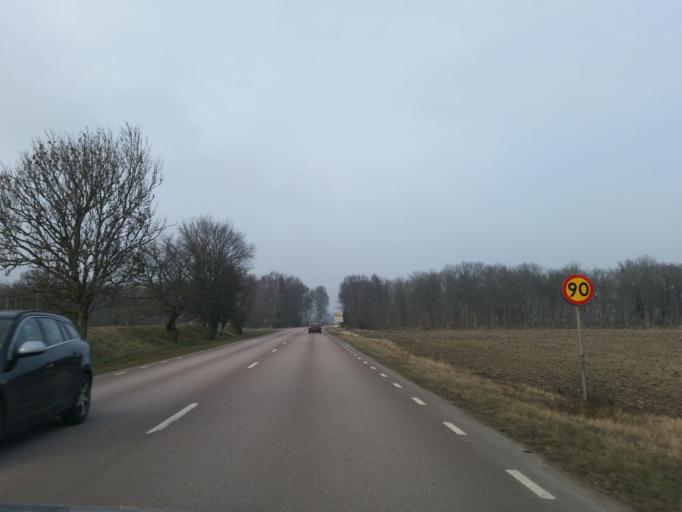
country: SE
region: Kalmar
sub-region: Borgholms Kommun
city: Borgholm
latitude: 57.1662
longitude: 17.0157
